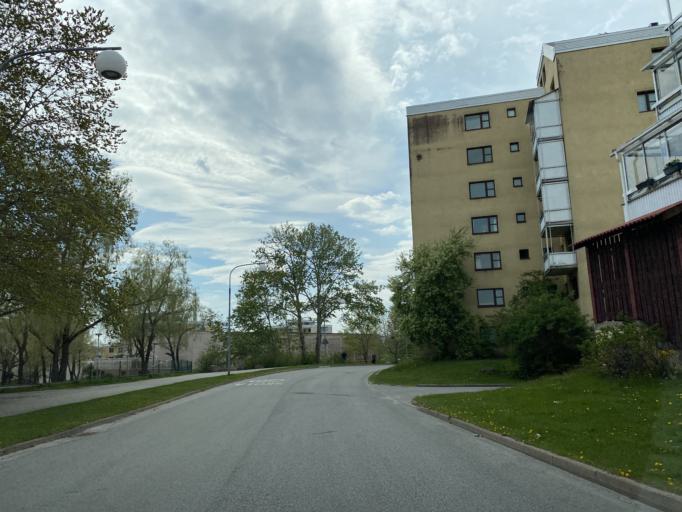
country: SE
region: Stockholm
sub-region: Stockholms Kommun
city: Kista
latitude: 59.4021
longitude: 17.9391
